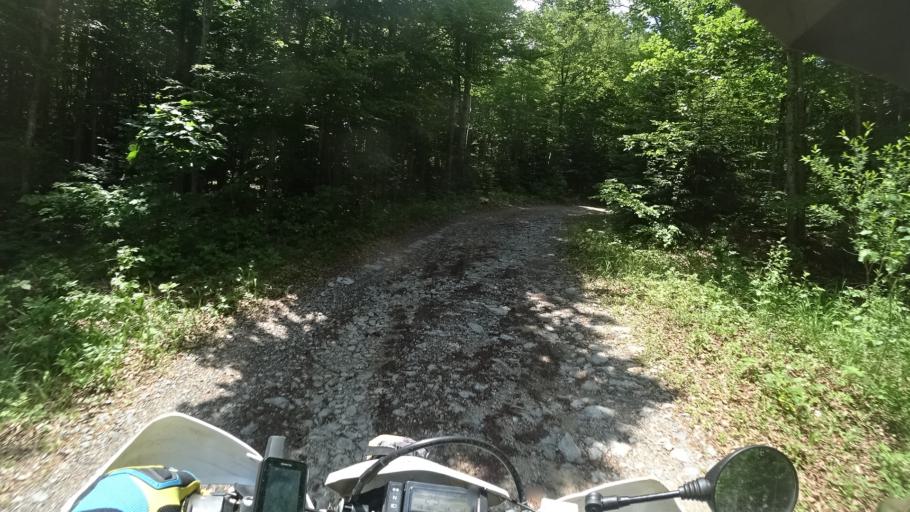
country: HR
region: Zadarska
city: Gracac
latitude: 44.4916
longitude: 15.8759
